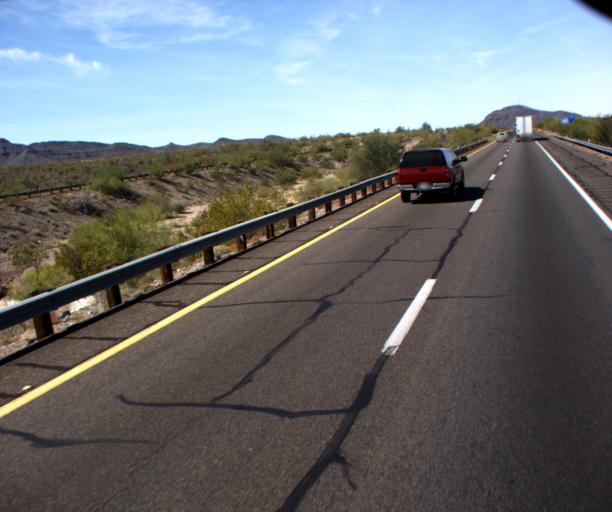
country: US
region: Arizona
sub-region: La Paz County
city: Quartzsite
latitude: 33.6604
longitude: -113.9970
